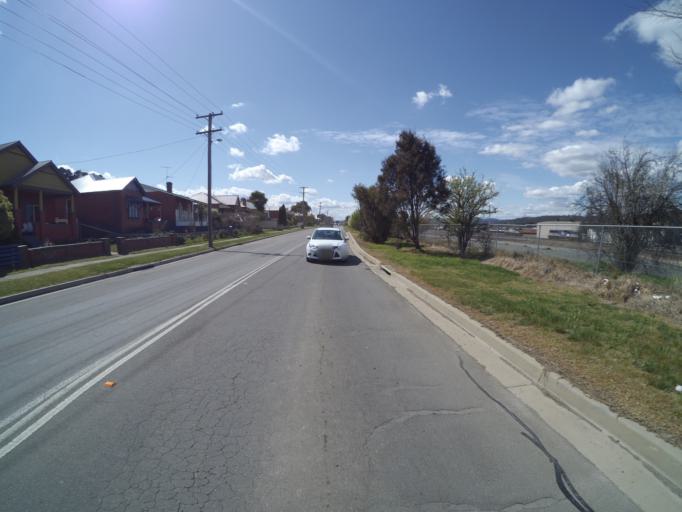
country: AU
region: New South Wales
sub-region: Goulburn Mulwaree
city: Goulburn
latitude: -34.7705
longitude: 149.7104
